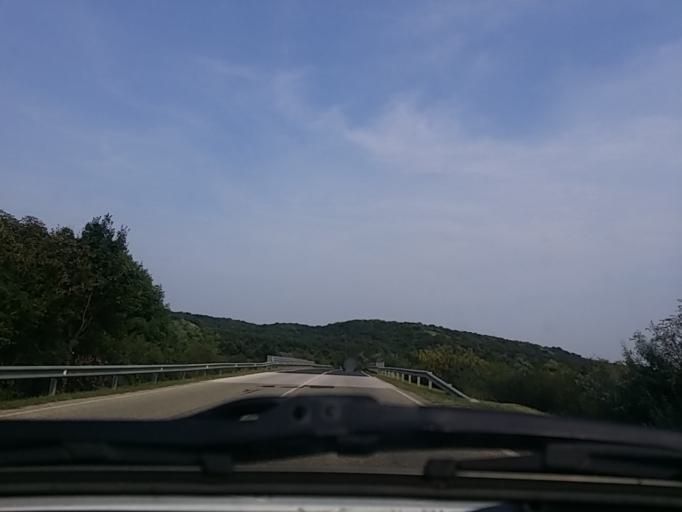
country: HU
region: Fejer
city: Szarliget
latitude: 47.4923
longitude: 18.5173
